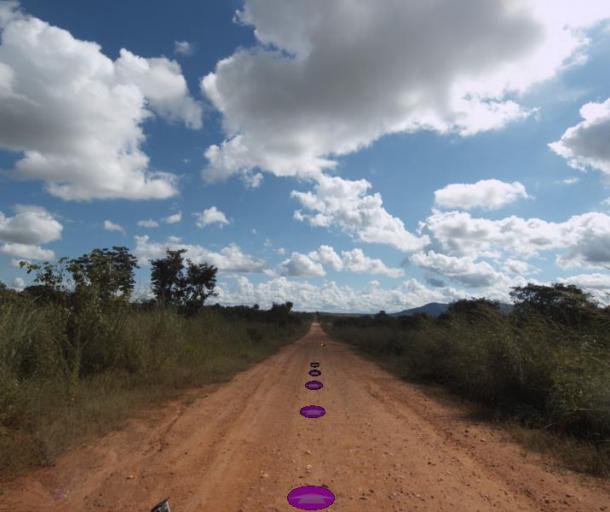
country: BR
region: Goias
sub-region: Jaragua
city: Jaragua
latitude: -15.8222
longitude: -49.2252
